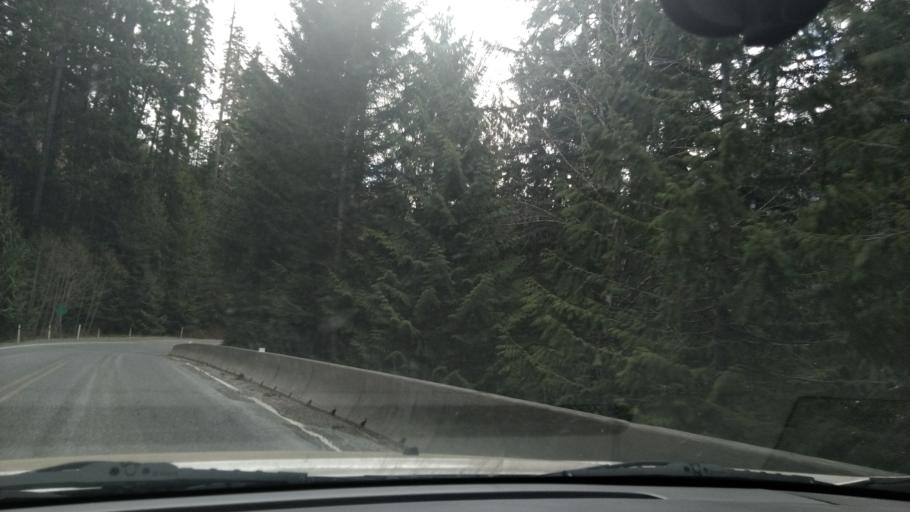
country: CA
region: British Columbia
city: Campbell River
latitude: 49.8485
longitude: -125.6260
